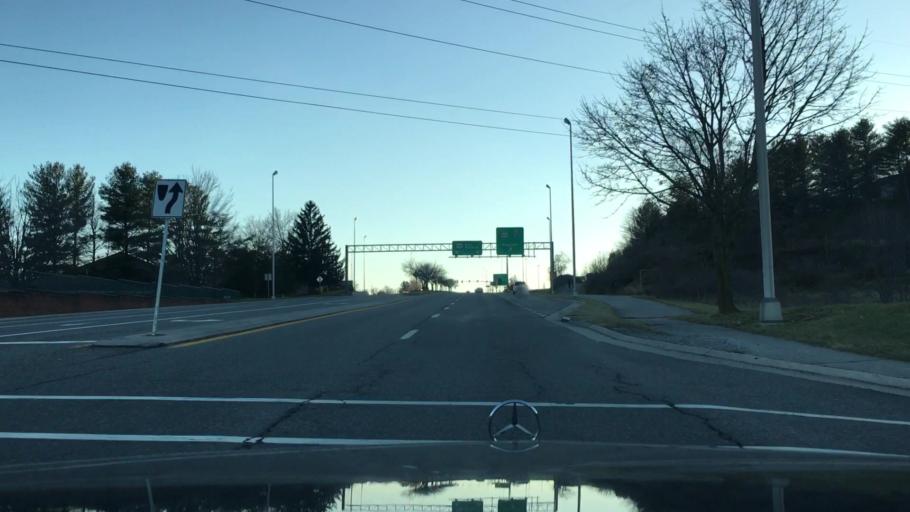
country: US
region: Virginia
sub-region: Montgomery County
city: Merrimac
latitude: 37.1976
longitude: -80.4015
